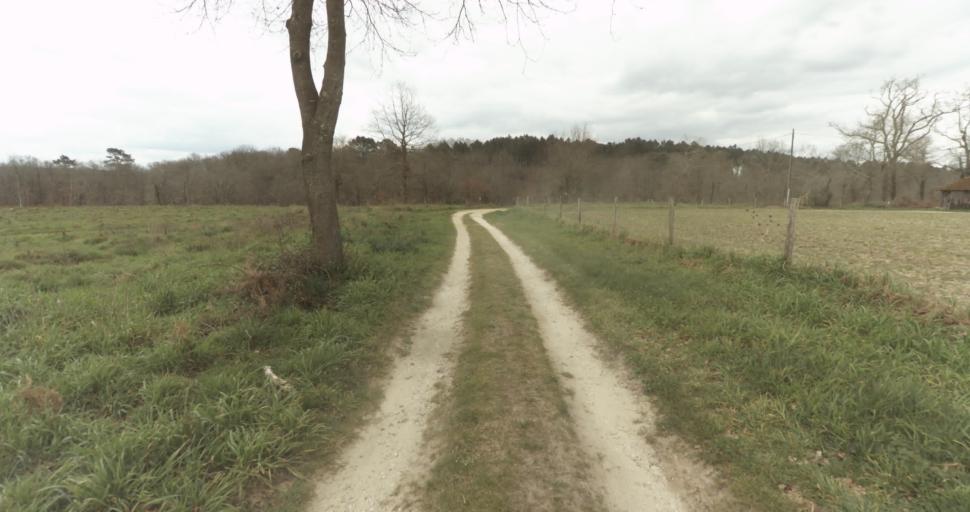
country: FR
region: Aquitaine
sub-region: Departement des Landes
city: Sarbazan
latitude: 44.0254
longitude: -0.3086
